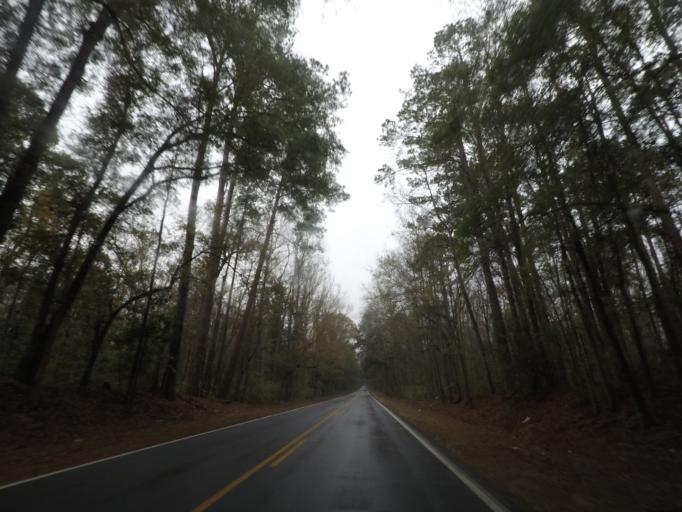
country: US
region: South Carolina
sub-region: Charleston County
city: Meggett
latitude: 32.7004
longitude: -80.3479
